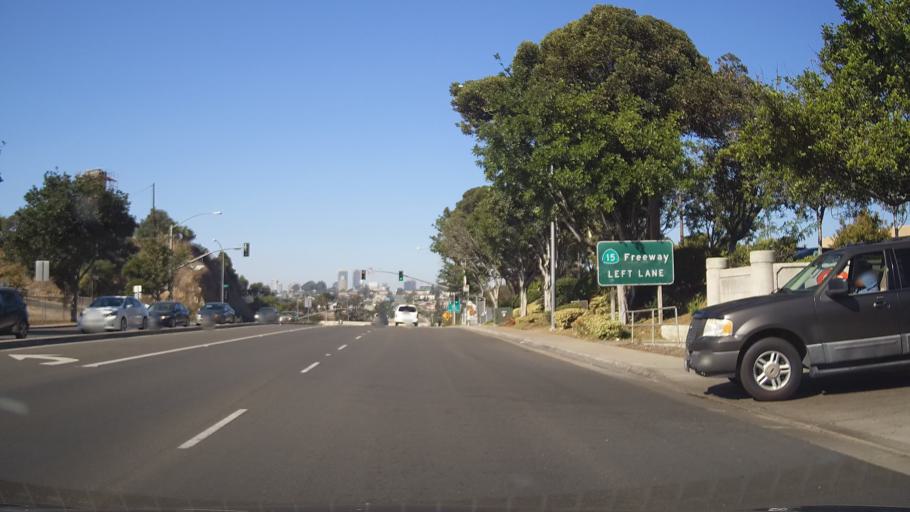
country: US
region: California
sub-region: San Diego County
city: National City
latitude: 32.7114
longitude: -117.1161
